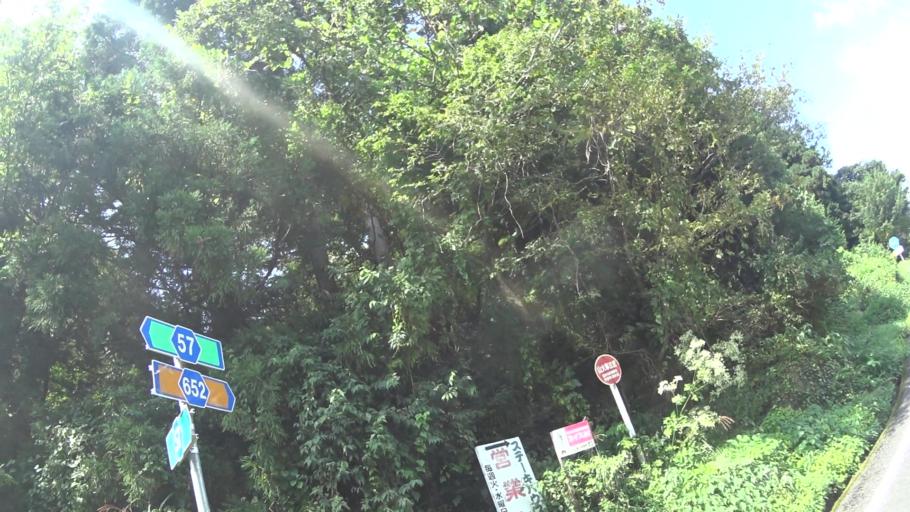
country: JP
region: Kyoto
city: Miyazu
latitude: 35.7218
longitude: 135.2114
